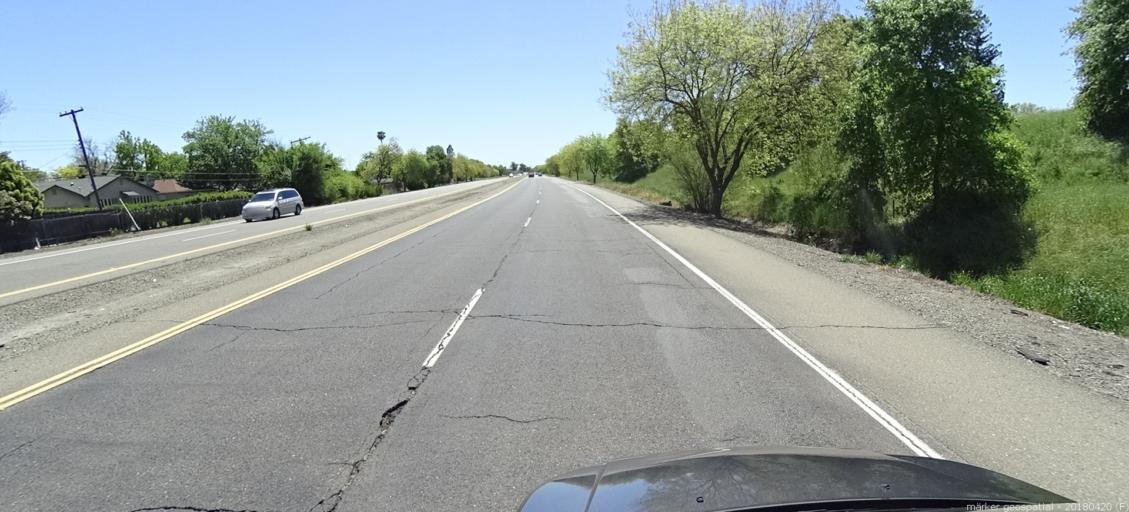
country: US
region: California
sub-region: Sacramento County
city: Parkway
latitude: 38.4894
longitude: -121.5063
